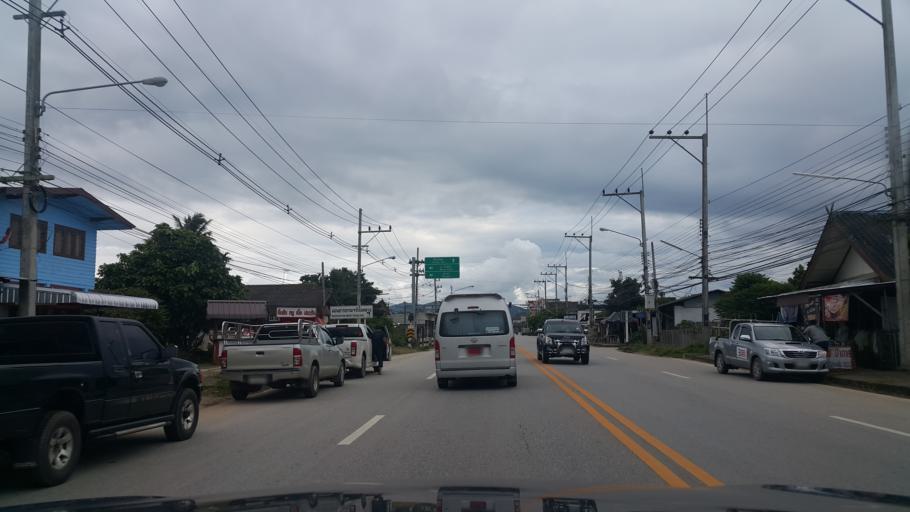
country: TH
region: Lampang
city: Wang Nuea
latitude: 19.2132
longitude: 99.5177
